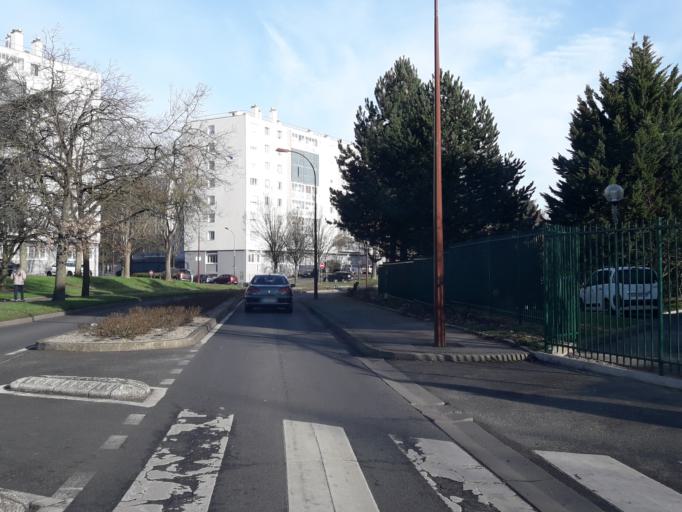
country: FR
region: Ile-de-France
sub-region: Departement de l'Essonne
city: Fleury-Merogis
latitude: 48.6401
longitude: 2.3487
